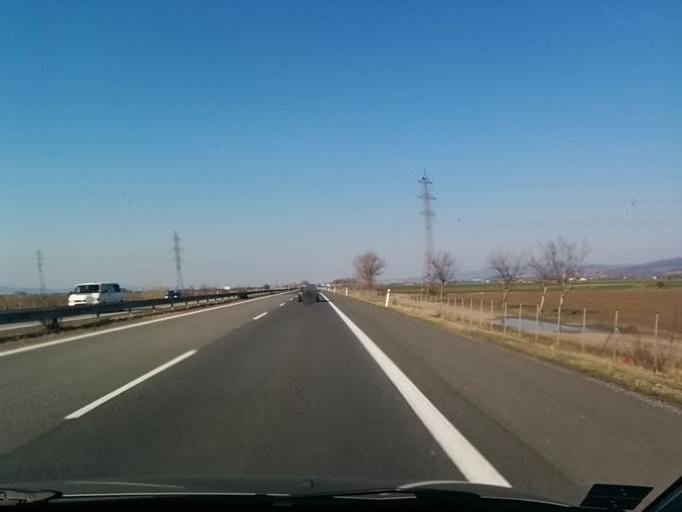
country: SK
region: Trnavsky
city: Leopoldov
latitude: 48.5251
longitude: 17.7793
